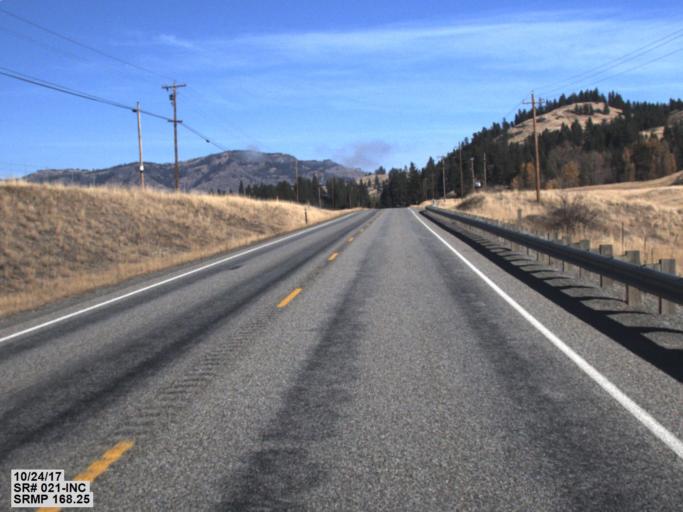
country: US
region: Washington
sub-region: Ferry County
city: Republic
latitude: 48.7193
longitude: -118.6547
